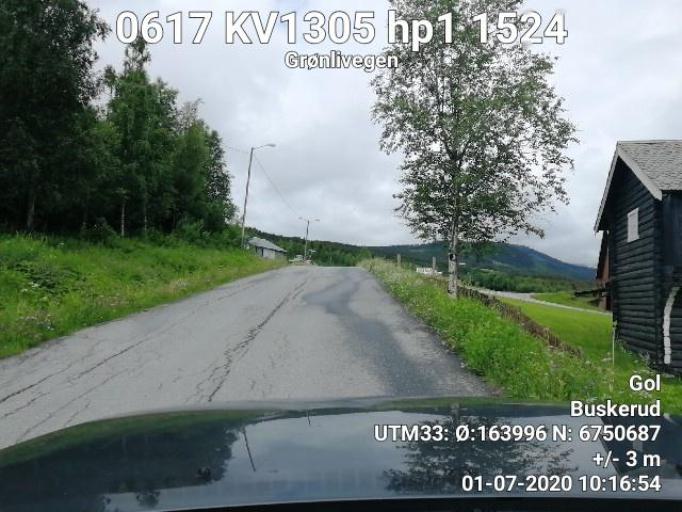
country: NO
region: Buskerud
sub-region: Gol
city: Gol
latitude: 60.7494
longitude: 8.8298
